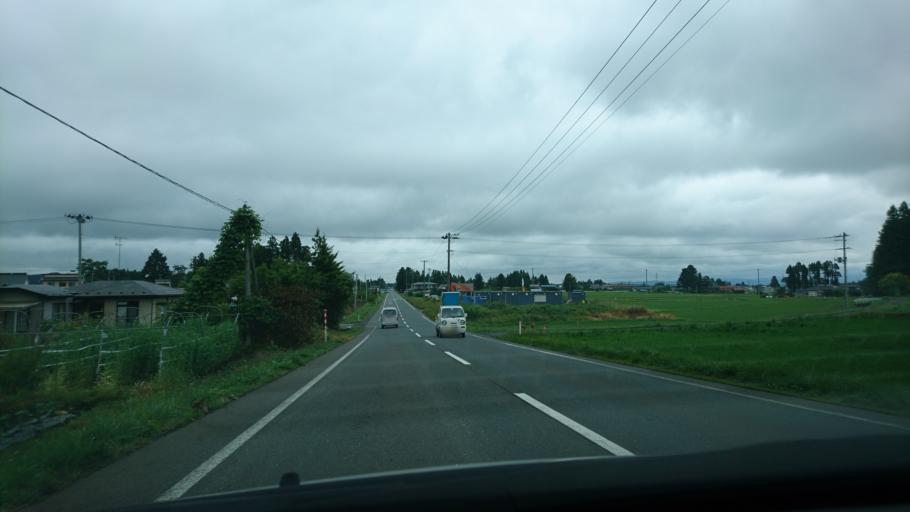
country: JP
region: Iwate
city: Mizusawa
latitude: 39.1199
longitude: 141.0528
